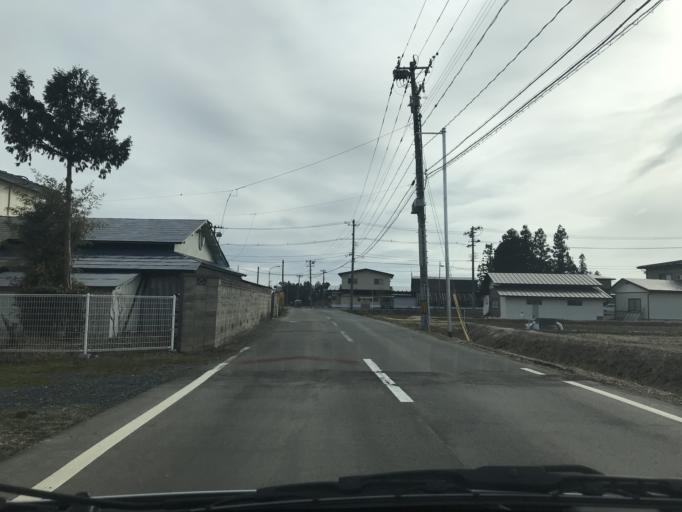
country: JP
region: Iwate
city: Hanamaki
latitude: 39.3995
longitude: 141.0752
